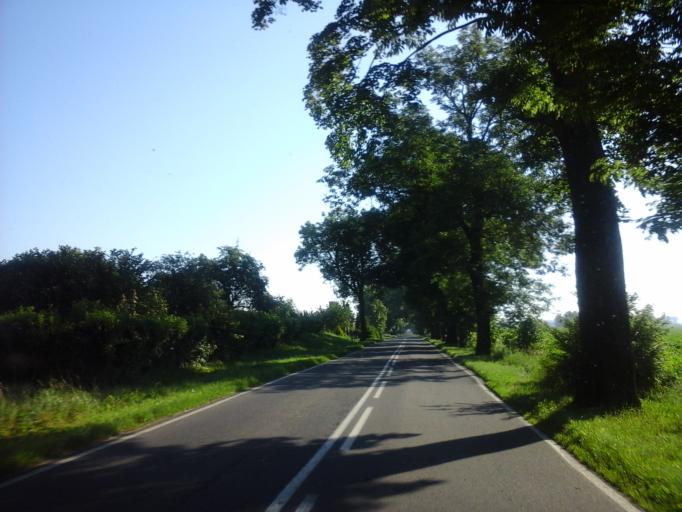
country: PL
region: West Pomeranian Voivodeship
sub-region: Powiat choszczenski
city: Choszczno
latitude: 53.1926
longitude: 15.4371
